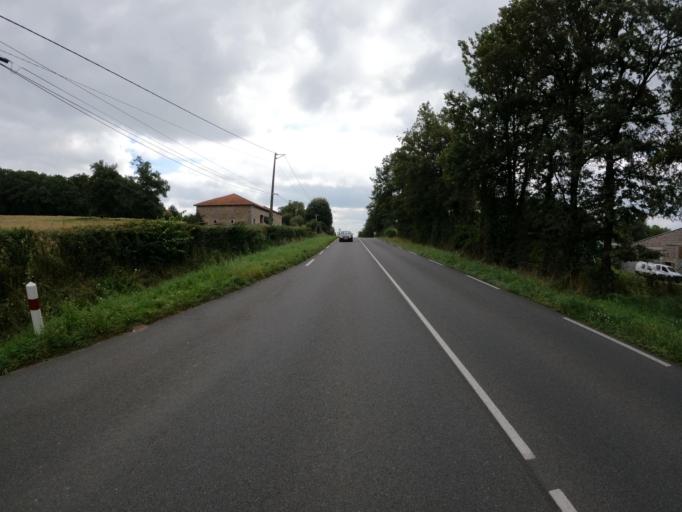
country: FR
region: Poitou-Charentes
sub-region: Departement de la Charente
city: Etagnac
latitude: 45.9027
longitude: 0.7648
